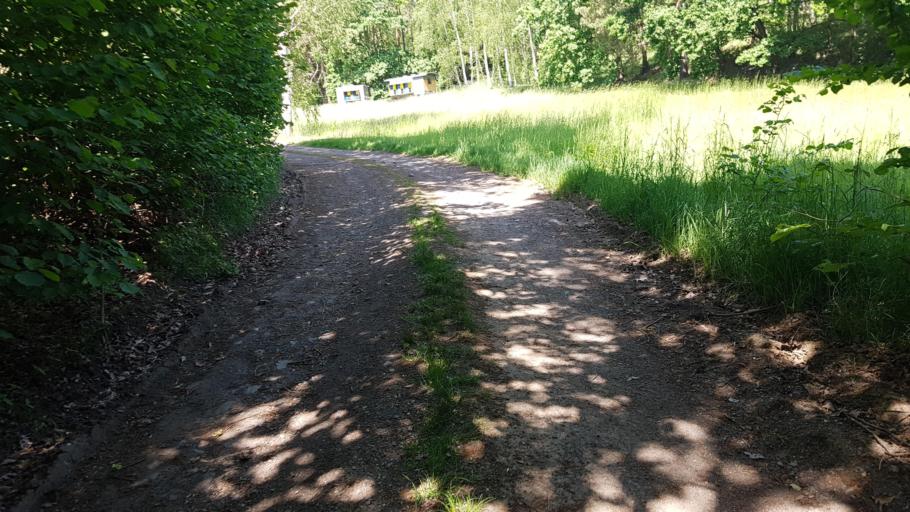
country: DE
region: Brandenburg
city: Grosskmehlen
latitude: 51.3647
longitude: 13.7084
